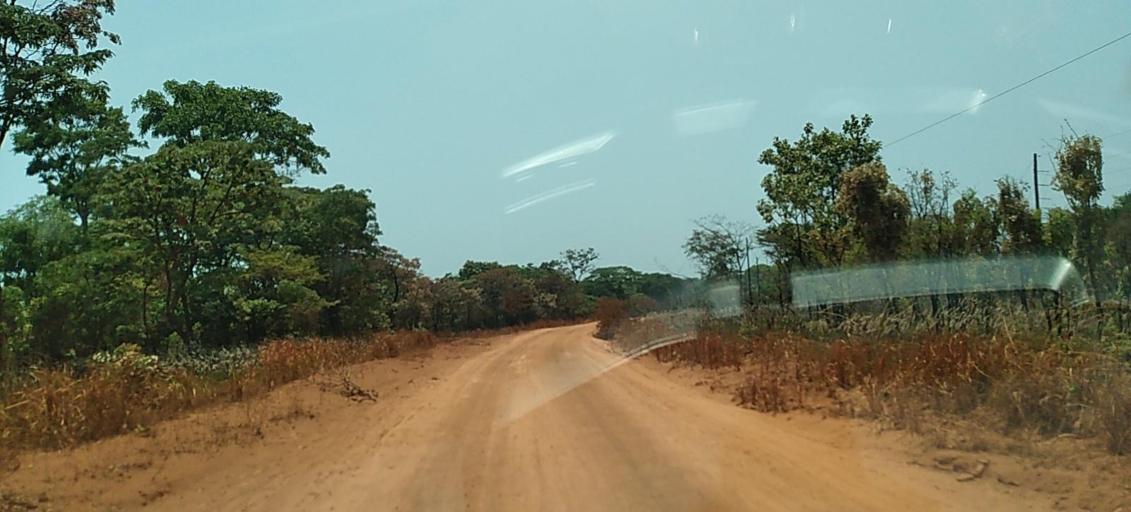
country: CD
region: Katanga
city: Kipushi
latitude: -11.9246
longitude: 27.0076
